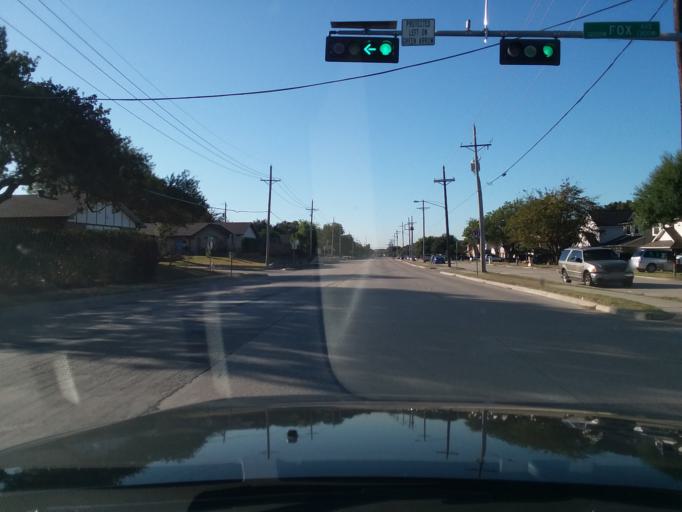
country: US
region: Texas
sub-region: Denton County
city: Lewisville
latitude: 33.0353
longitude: -97.0276
